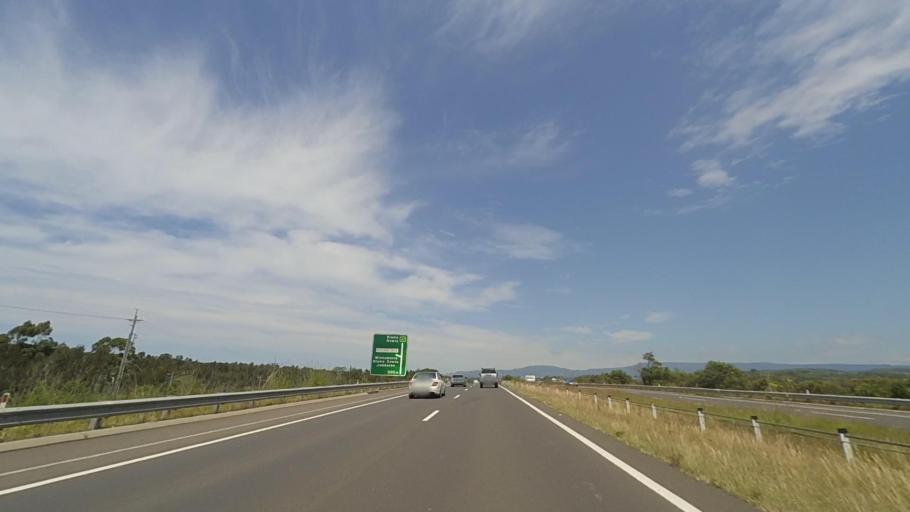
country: AU
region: New South Wales
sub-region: Shellharbour
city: Croom
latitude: -34.6073
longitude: 150.8387
